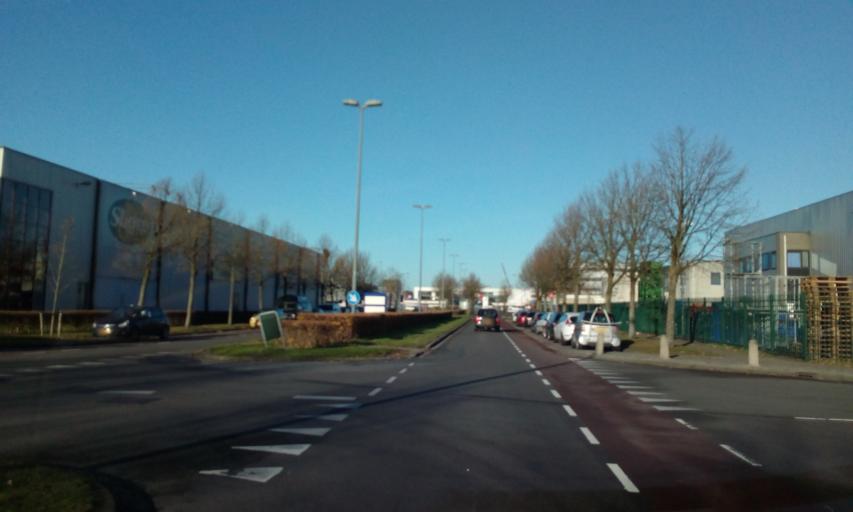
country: NL
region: South Holland
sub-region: Gemeente Leidschendam-Voorburg
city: Voorburg
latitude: 52.0675
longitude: 4.3923
